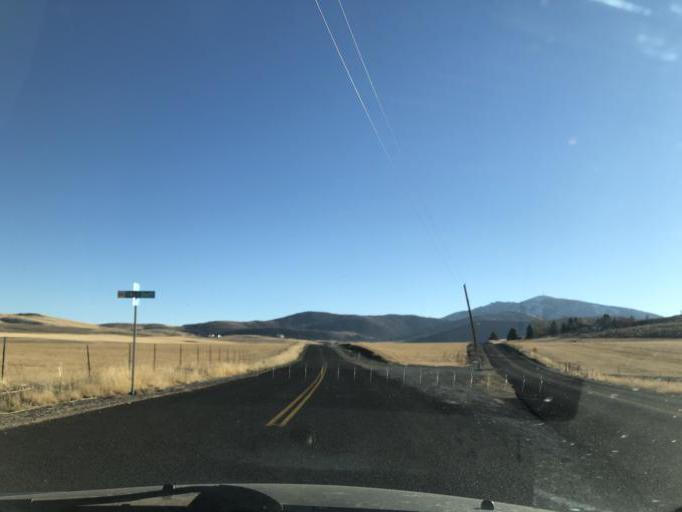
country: US
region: Utah
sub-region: Cache County
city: Wellsville
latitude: 41.5996
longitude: -111.9297
